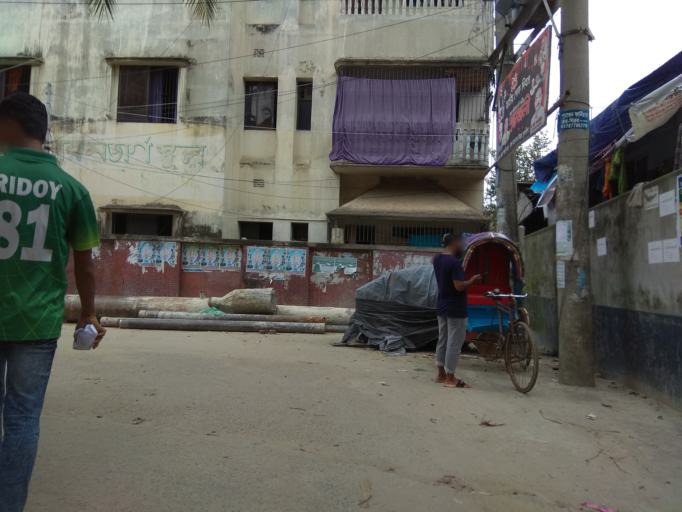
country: BD
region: Dhaka
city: Tungi
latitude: 23.8159
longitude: 90.3763
